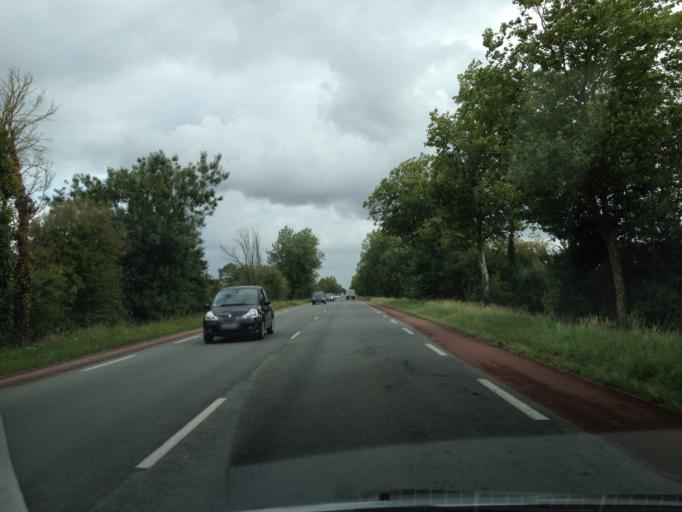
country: FR
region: Poitou-Charentes
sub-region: Departement de la Charente-Maritime
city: Marans
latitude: 46.2774
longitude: -0.9987
